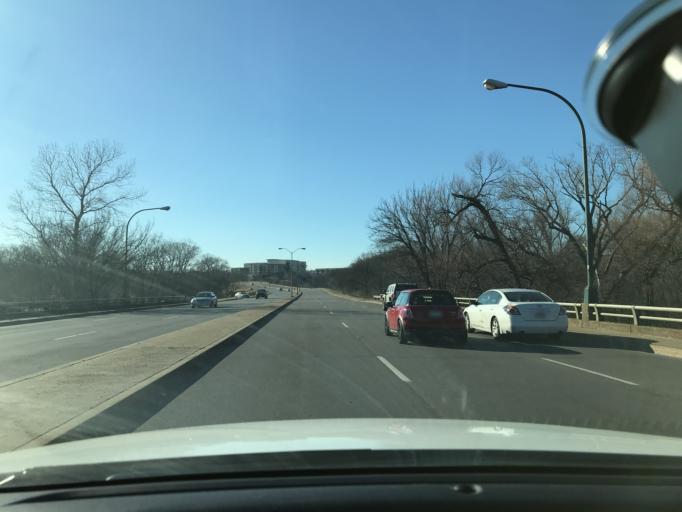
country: US
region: Texas
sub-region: Dallas County
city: Highland Park
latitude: 32.8528
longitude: -96.7230
